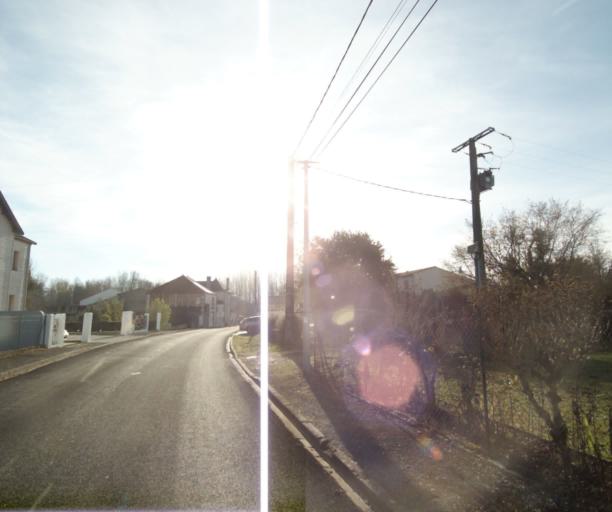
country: FR
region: Poitou-Charentes
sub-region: Departement de la Charente-Maritime
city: Chaniers
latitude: 45.7095
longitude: -0.5277
